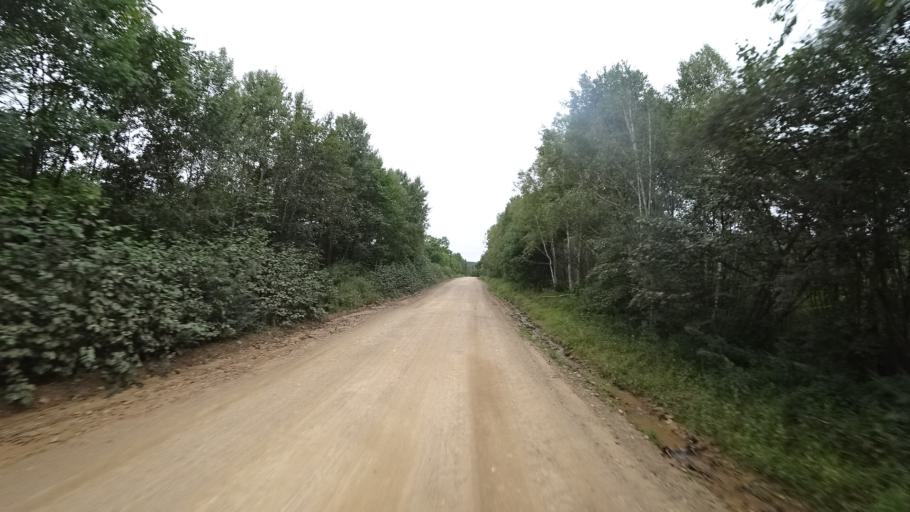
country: RU
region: Primorskiy
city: Rettikhovka
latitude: 44.1783
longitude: 132.8031
